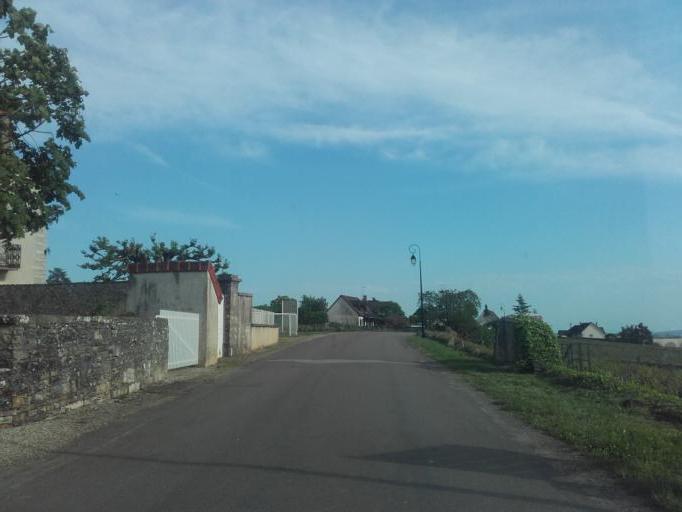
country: FR
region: Bourgogne
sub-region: Departement de la Cote-d'Or
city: Meursault
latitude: 46.9907
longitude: 4.7666
